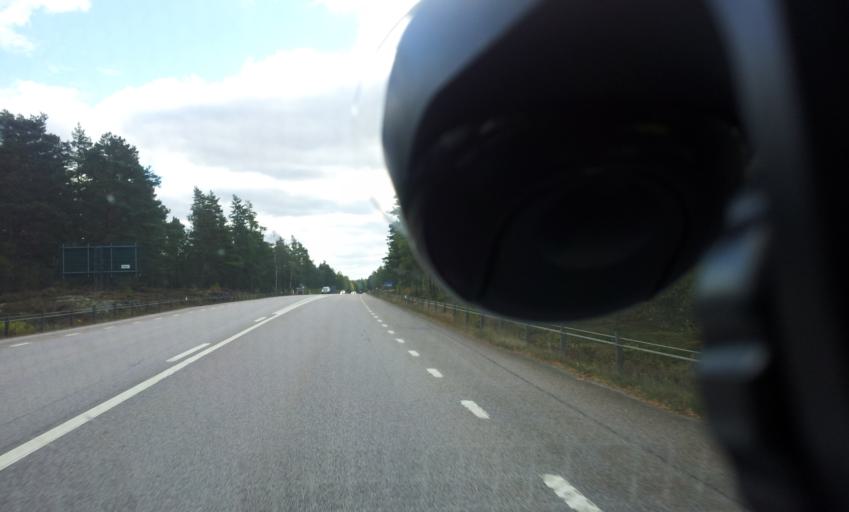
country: SE
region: Kalmar
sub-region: Vasterviks Kommun
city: Ankarsrum
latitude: 57.5271
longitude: 16.4904
